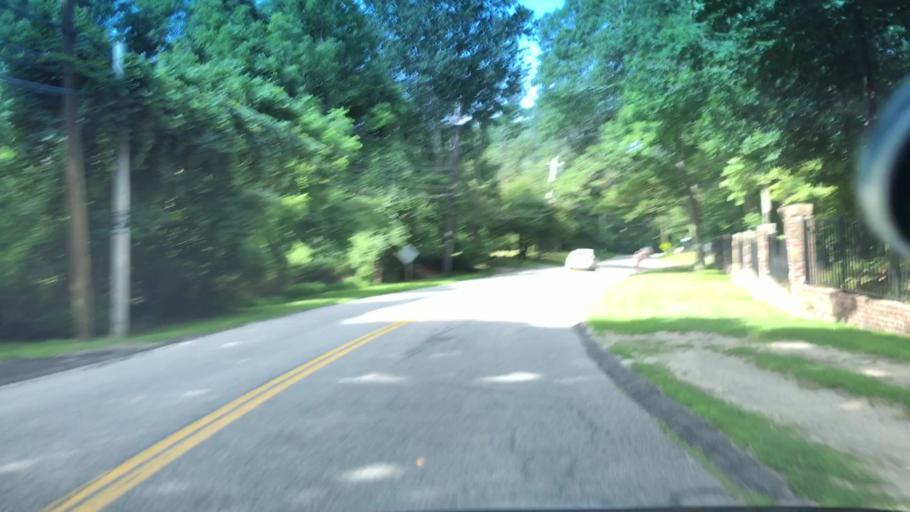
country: US
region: New York
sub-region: Suffolk County
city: Wading River
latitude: 40.9596
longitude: -72.8345
